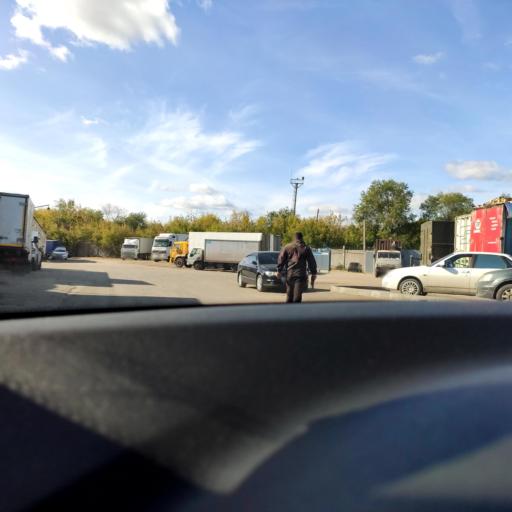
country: RU
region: Samara
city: Petra-Dubrava
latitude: 53.2546
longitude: 50.2937
